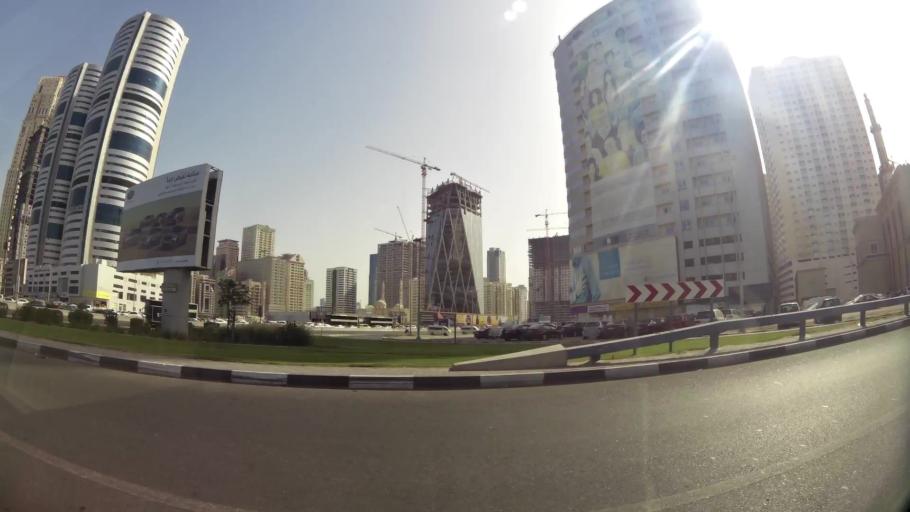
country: AE
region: Ash Shariqah
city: Sharjah
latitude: 25.3008
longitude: 55.3653
